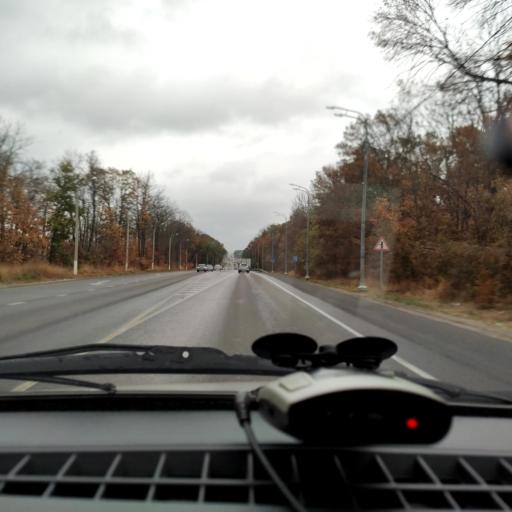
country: RU
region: Voronezj
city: Semiluki
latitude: 51.6387
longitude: 39.0086
